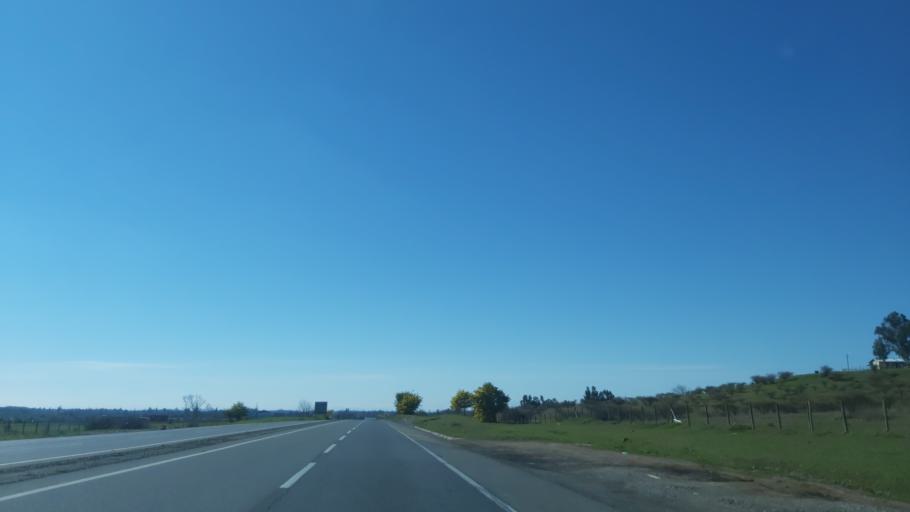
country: CL
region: Biobio
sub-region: Provincia de Nuble
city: Bulnes
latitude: -36.6598
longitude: -72.2550
